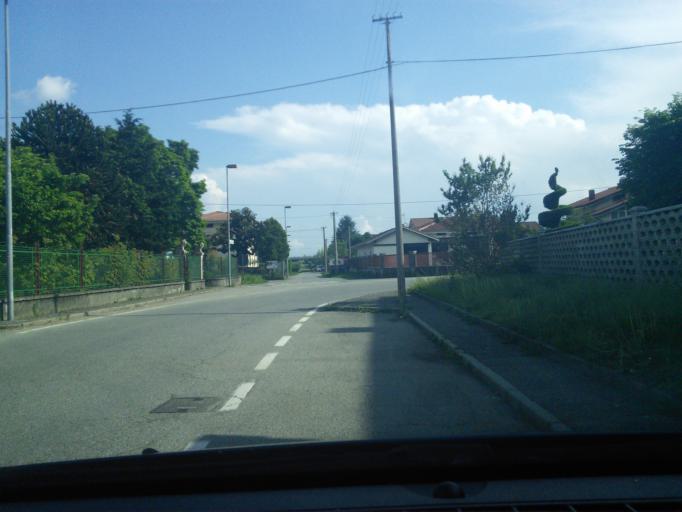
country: IT
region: Piedmont
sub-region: Provincia di Torino
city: Quassolo
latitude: 45.5069
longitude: 7.8294
